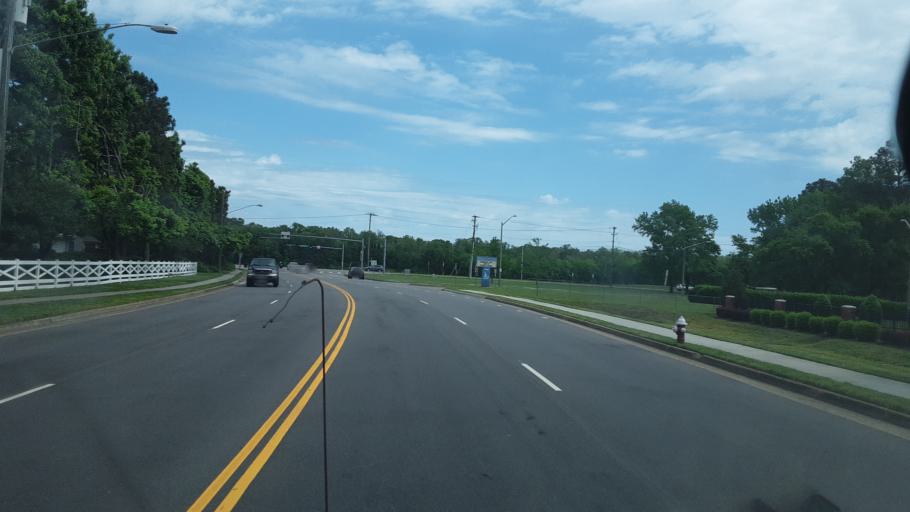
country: US
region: Virginia
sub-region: City of Virginia Beach
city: Virginia Beach
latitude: 36.7843
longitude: -75.9934
